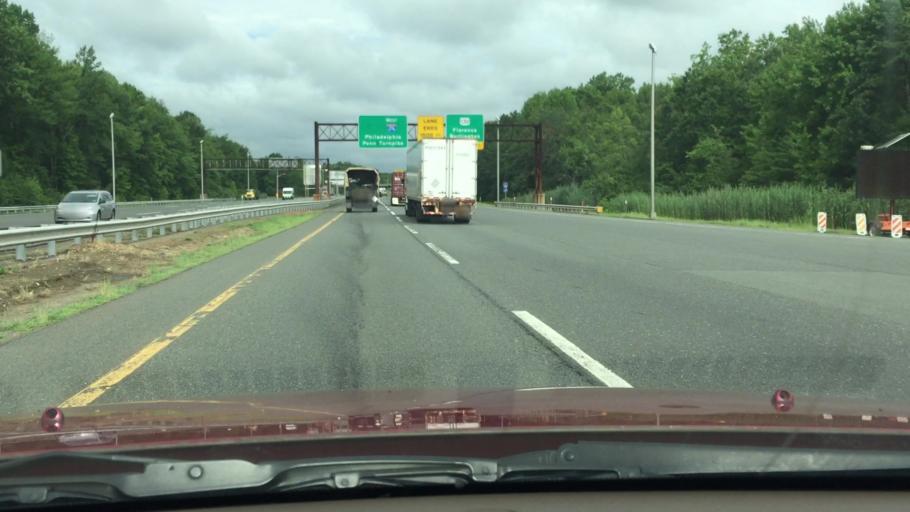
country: US
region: New Jersey
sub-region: Burlington County
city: Roebling
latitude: 40.0976
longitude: -74.7807
